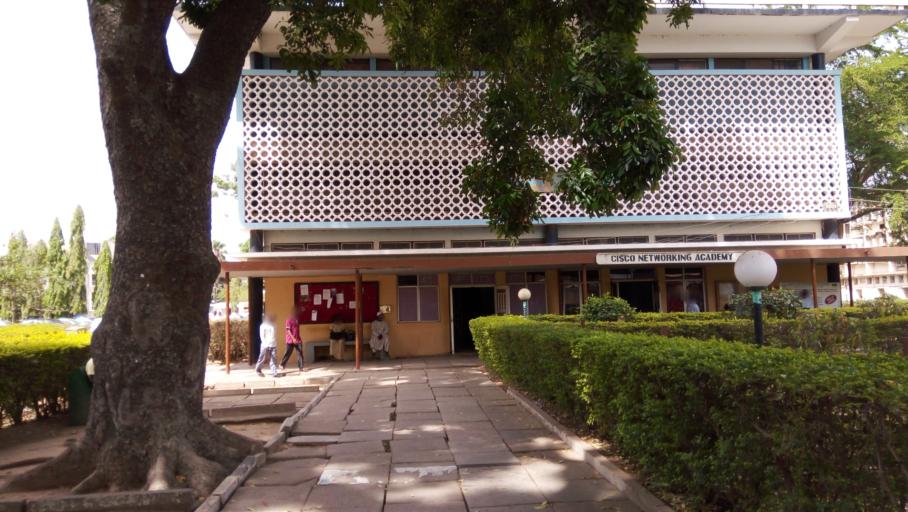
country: NG
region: Kaduna
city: Zaria
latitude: 11.1504
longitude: 7.6555
